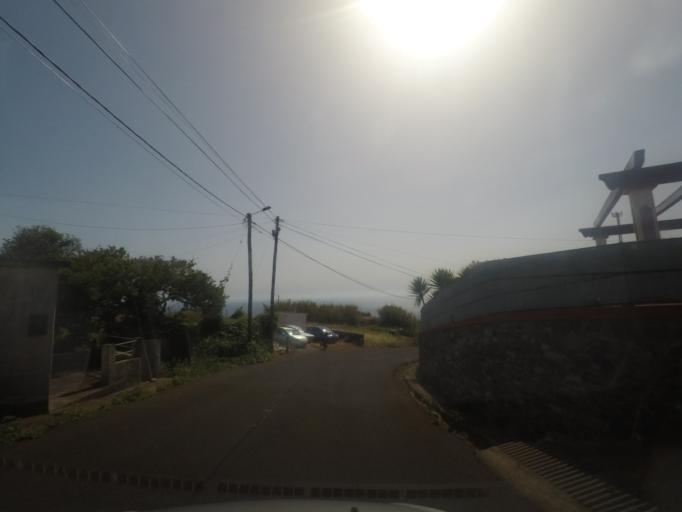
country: PT
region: Madeira
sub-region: Calheta
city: Faja da Ovelha
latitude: 32.8137
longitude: -17.2495
